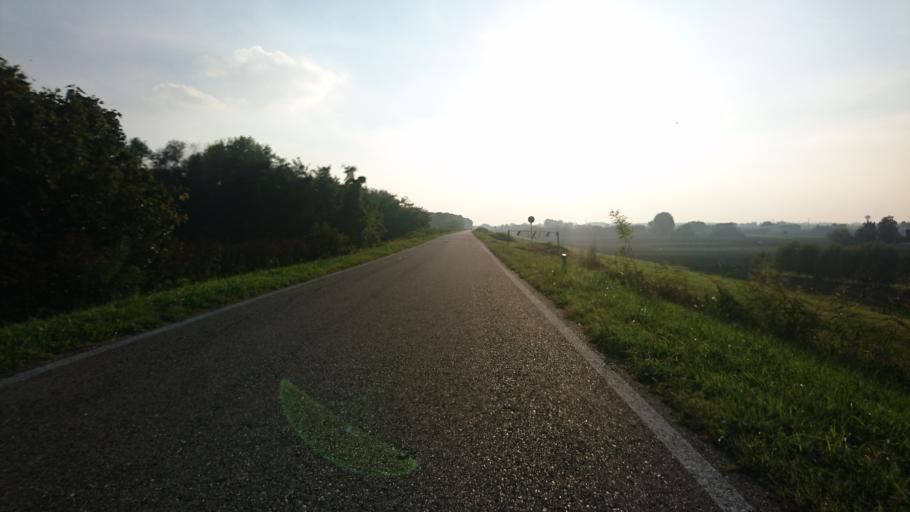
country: IT
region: Emilia-Romagna
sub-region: Provincia di Ferrara
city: Francolino
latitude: 44.8986
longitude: 11.6373
